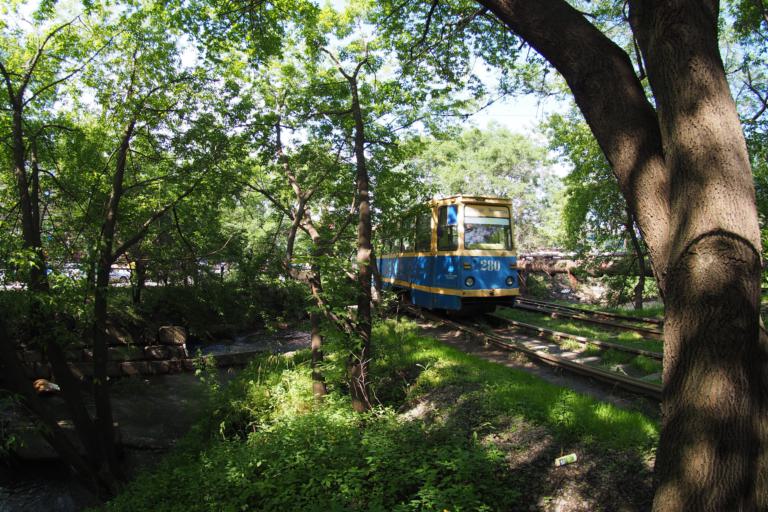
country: RU
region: Primorskiy
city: Vladivostok
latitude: 43.1041
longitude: 131.9378
